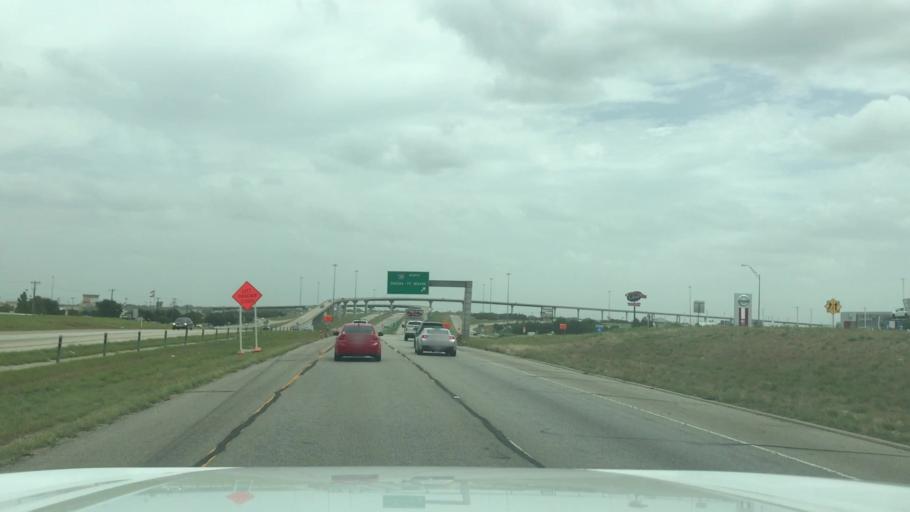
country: US
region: Texas
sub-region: McLennan County
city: Beverly Hills
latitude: 31.4973
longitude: -97.1616
